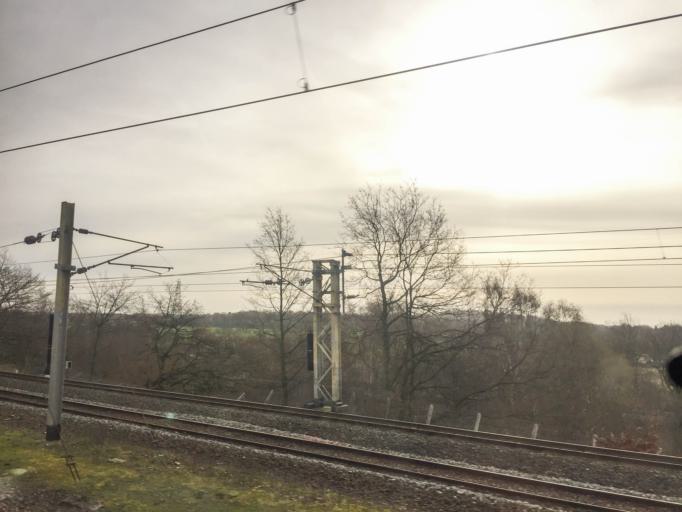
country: GB
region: England
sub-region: Borough of Halton
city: Daresbury
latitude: 53.3671
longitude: -2.6172
